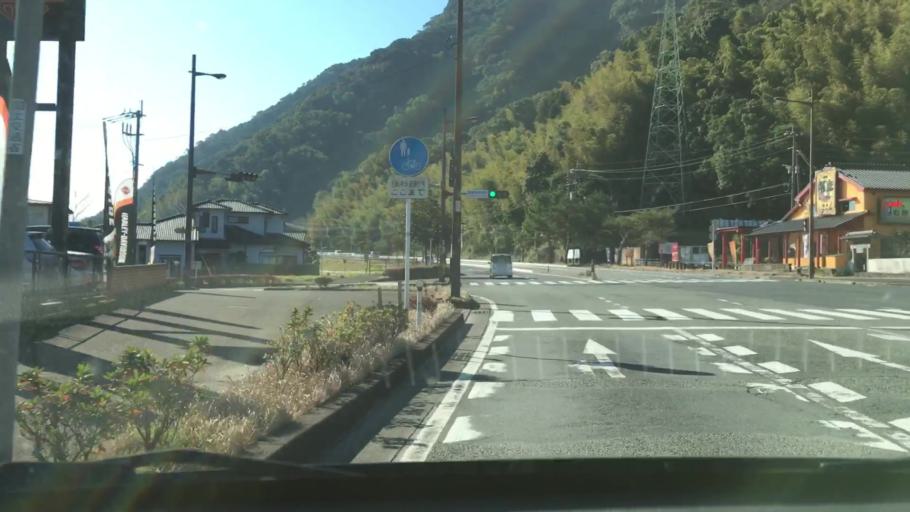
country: JP
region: Kagoshima
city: Kajiki
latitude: 31.7034
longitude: 130.6117
